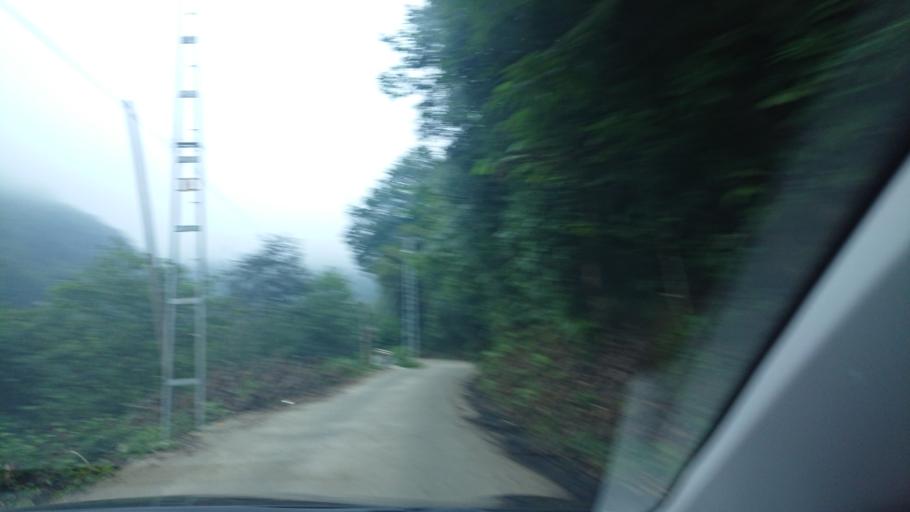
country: TR
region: Rize
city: Cayeli
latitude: 41.0463
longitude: 40.8011
